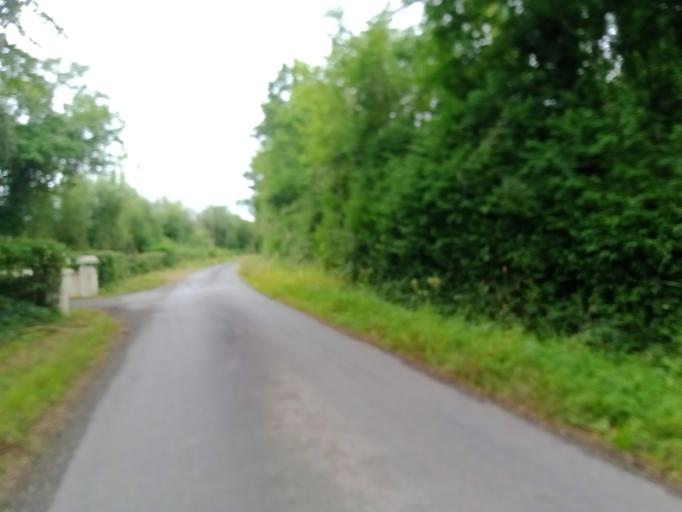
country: IE
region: Leinster
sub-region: Kilkenny
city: Callan
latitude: 52.5785
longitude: -7.4039
